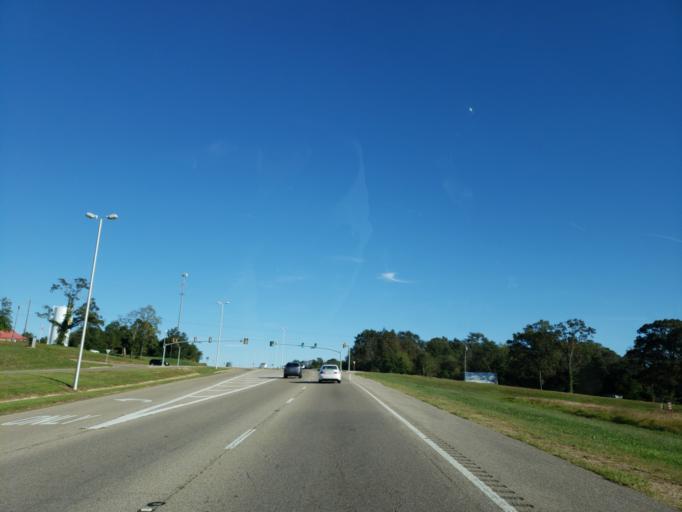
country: US
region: Mississippi
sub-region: Forrest County
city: Petal
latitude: 31.3542
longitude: -89.2535
